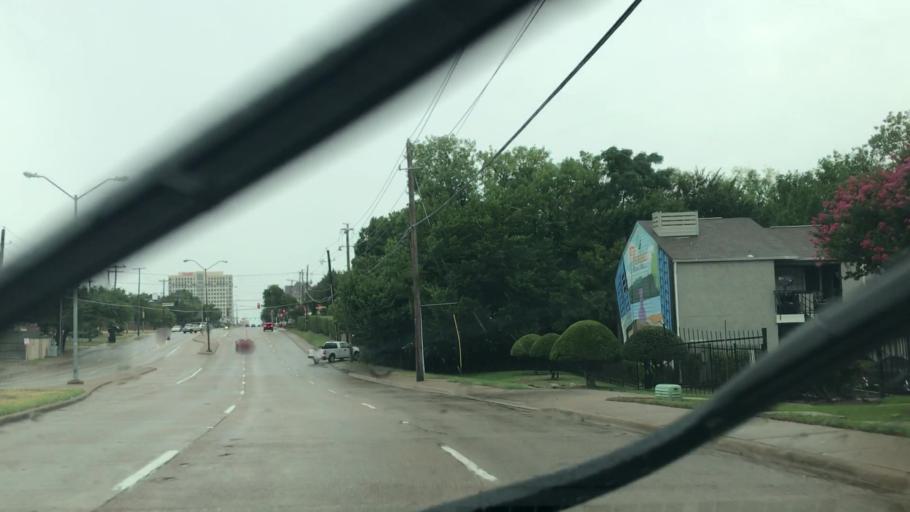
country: US
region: Texas
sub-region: Dallas County
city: Addison
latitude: 32.9396
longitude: -96.8118
